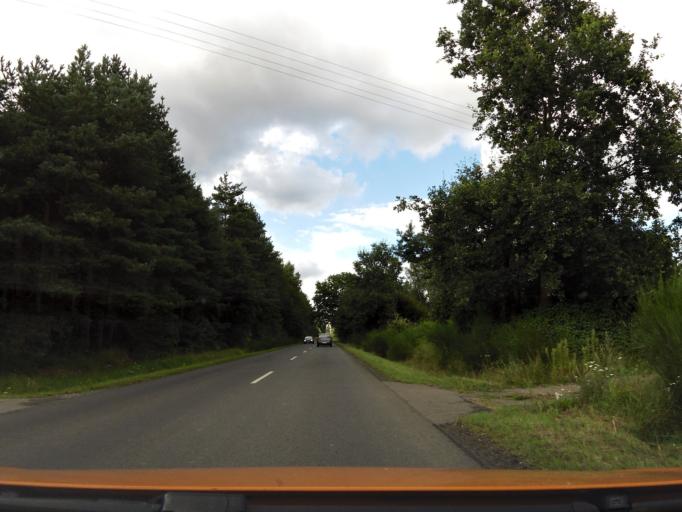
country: PL
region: West Pomeranian Voivodeship
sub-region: Powiat kolobrzeski
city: Ryman
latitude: 53.9640
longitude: 15.4916
